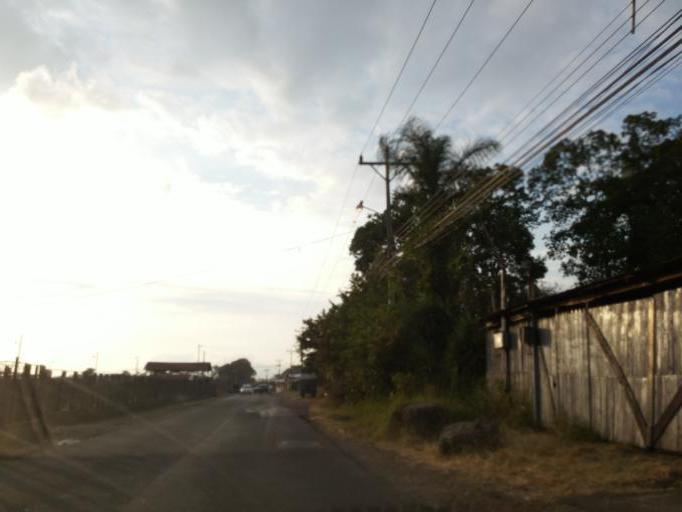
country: CR
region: Alajuela
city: Alajuela
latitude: 10.0052
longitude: -84.2288
